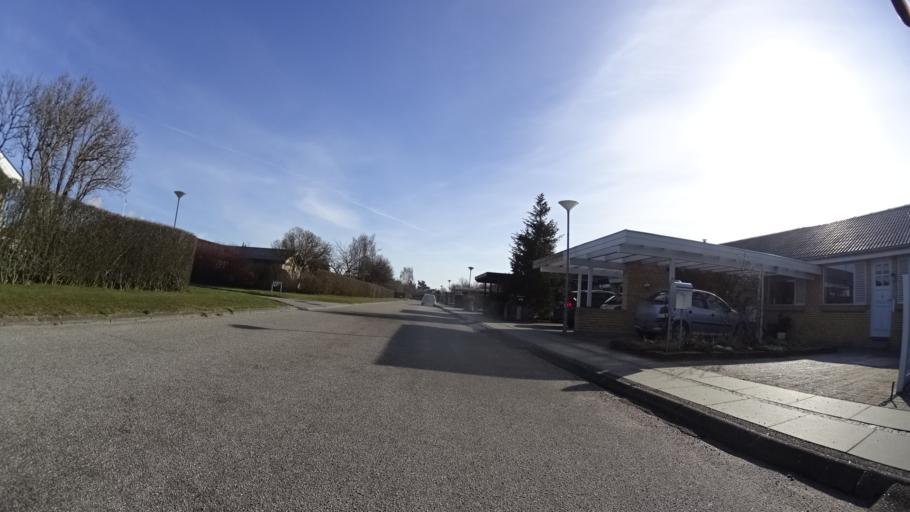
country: DK
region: Central Jutland
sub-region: Arhus Kommune
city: Tranbjerg
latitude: 56.0874
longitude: 10.1170
